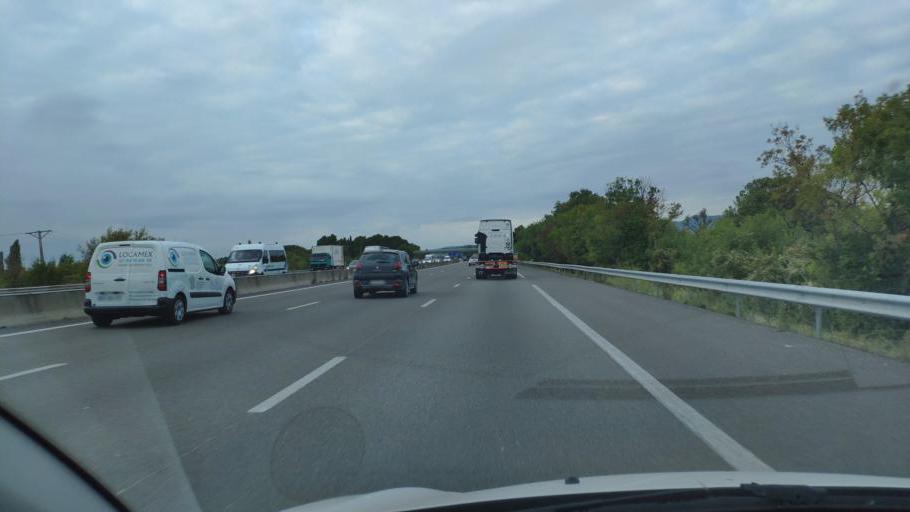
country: FR
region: Provence-Alpes-Cote d'Azur
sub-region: Departement des Bouches-du-Rhone
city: Pelissanne
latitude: 43.6115
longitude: 5.1491
